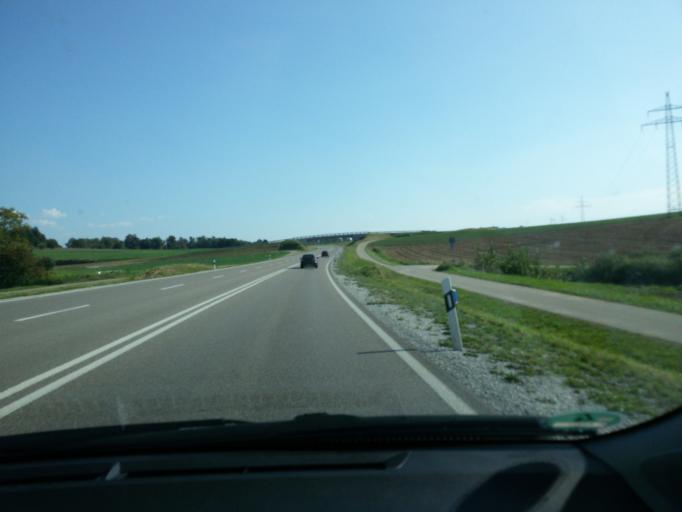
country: DE
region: Bavaria
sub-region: Swabia
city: Harburg
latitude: 48.7481
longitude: 10.7303
